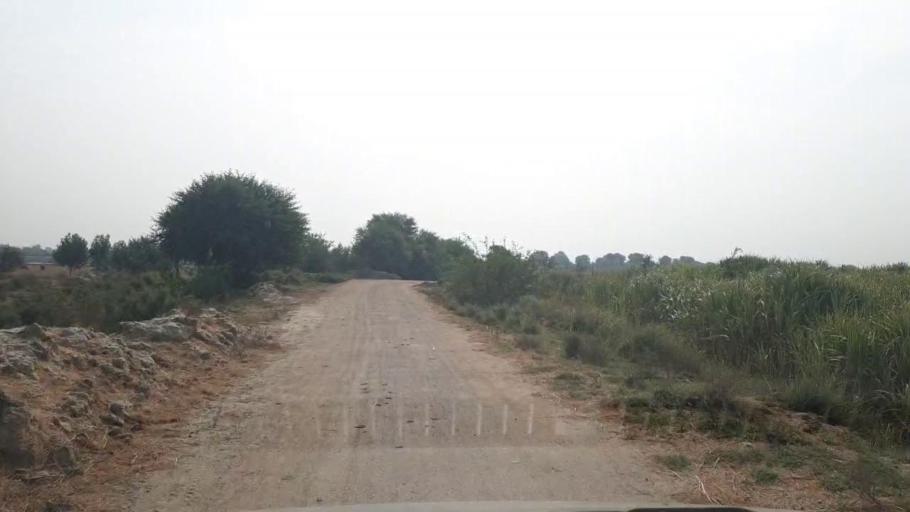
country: PK
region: Sindh
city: Tando Muhammad Khan
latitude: 25.1162
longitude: 68.4962
